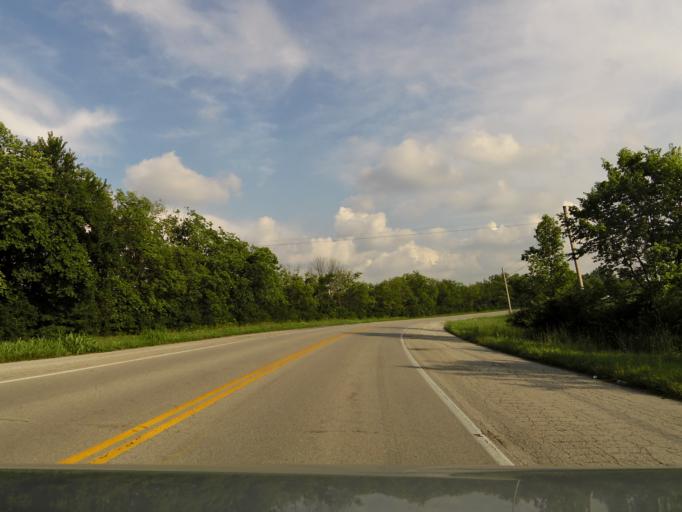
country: US
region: Kentucky
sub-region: Harrison County
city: Cynthiana
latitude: 38.2966
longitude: -84.3028
